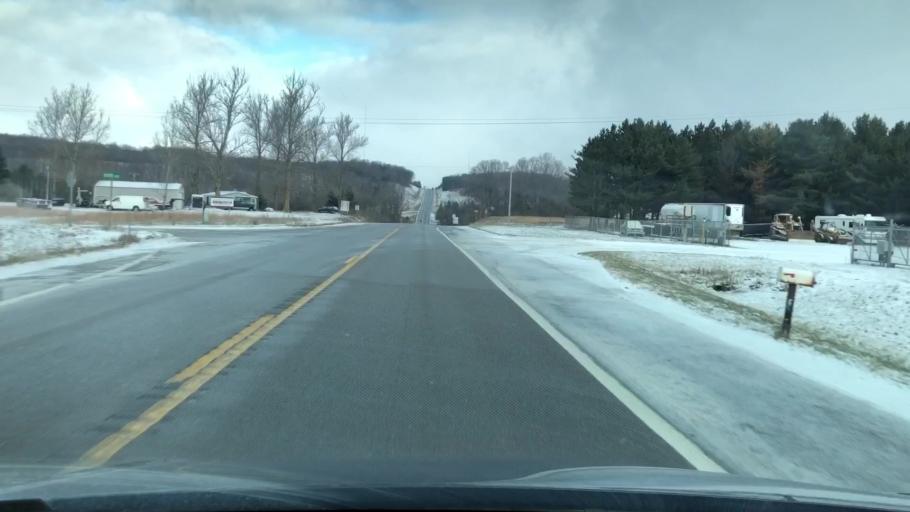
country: US
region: Michigan
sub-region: Grand Traverse County
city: Kingsley
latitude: 44.4321
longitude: -85.6985
